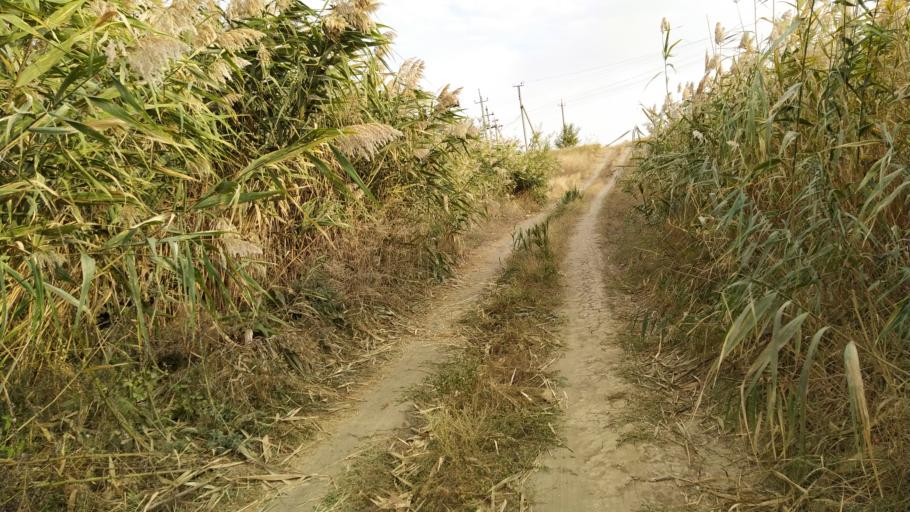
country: RU
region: Rostov
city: Kuleshovka
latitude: 47.1095
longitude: 39.6134
